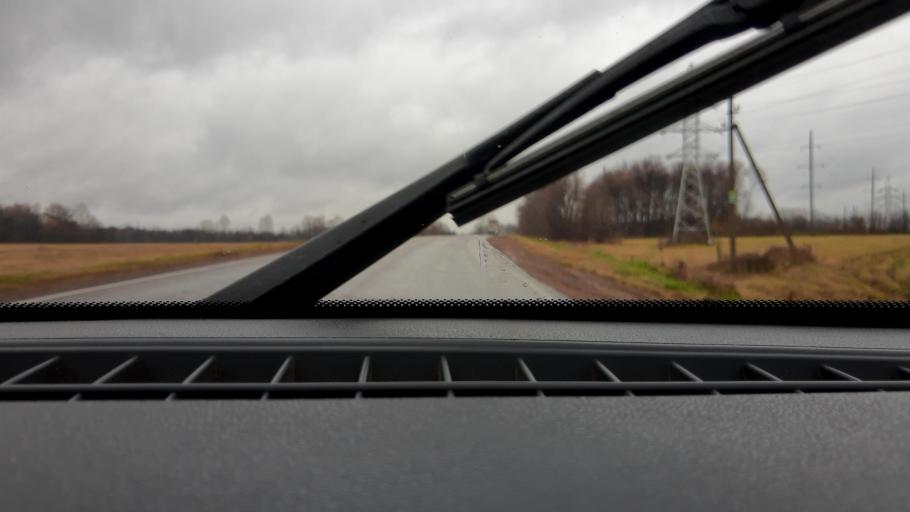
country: RU
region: Bashkortostan
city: Mikhaylovka
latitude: 54.8332
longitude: 55.7899
